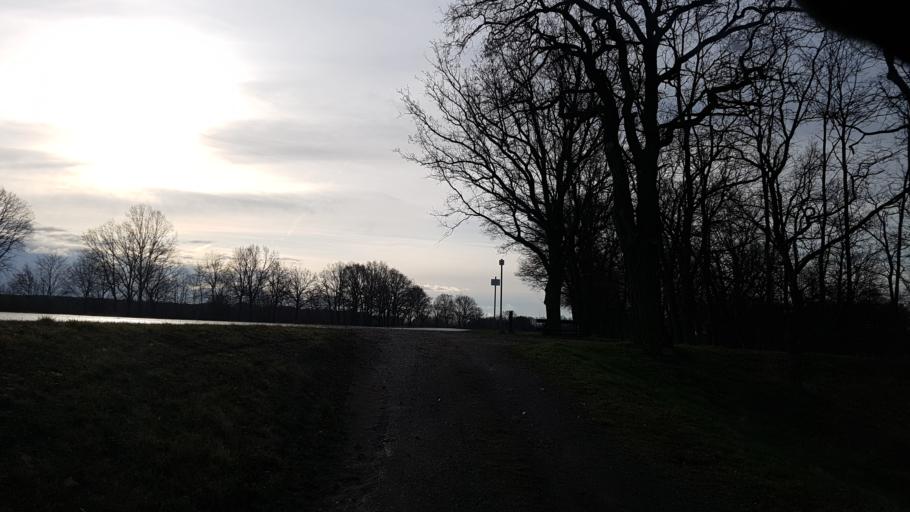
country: DE
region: Brandenburg
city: Herzberg
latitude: 51.6579
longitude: 13.2681
